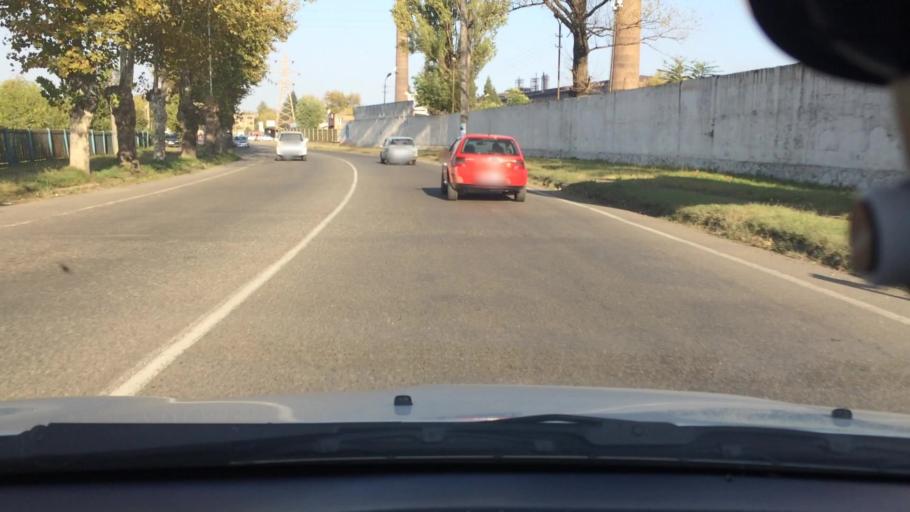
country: GE
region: Imereti
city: Zestap'oni
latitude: 42.1165
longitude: 43.0214
